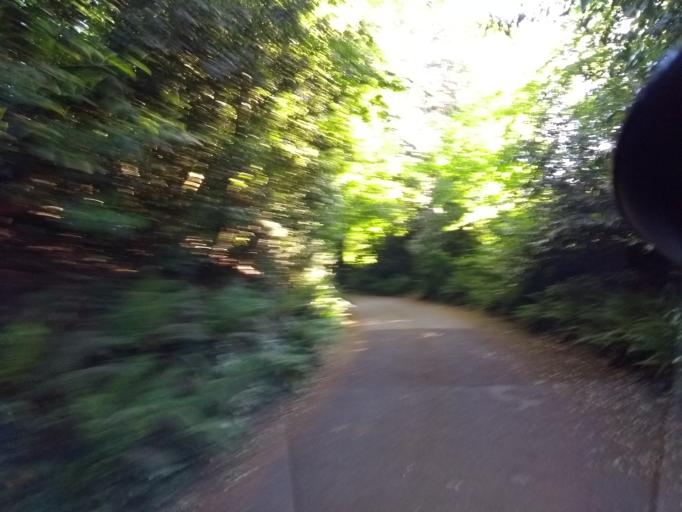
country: GB
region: England
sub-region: Somerset
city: Creech Saint Michael
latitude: 51.0510
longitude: -3.0546
